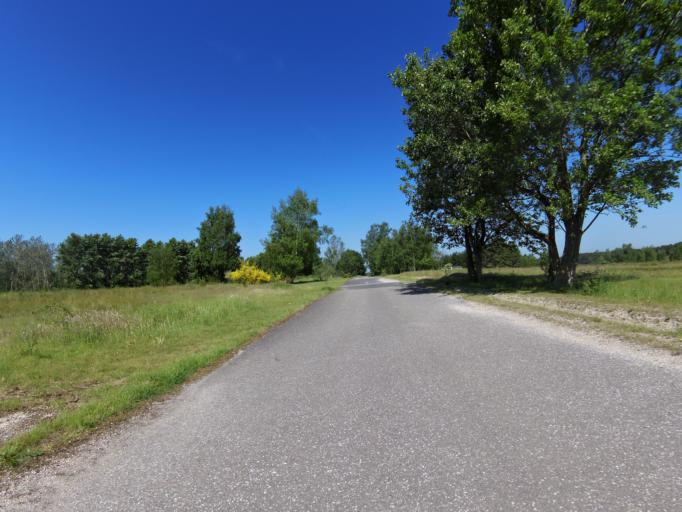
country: NL
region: Limburg
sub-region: Gemeente Onderbanken
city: Schinveld
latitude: 50.9354
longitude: 6.0372
